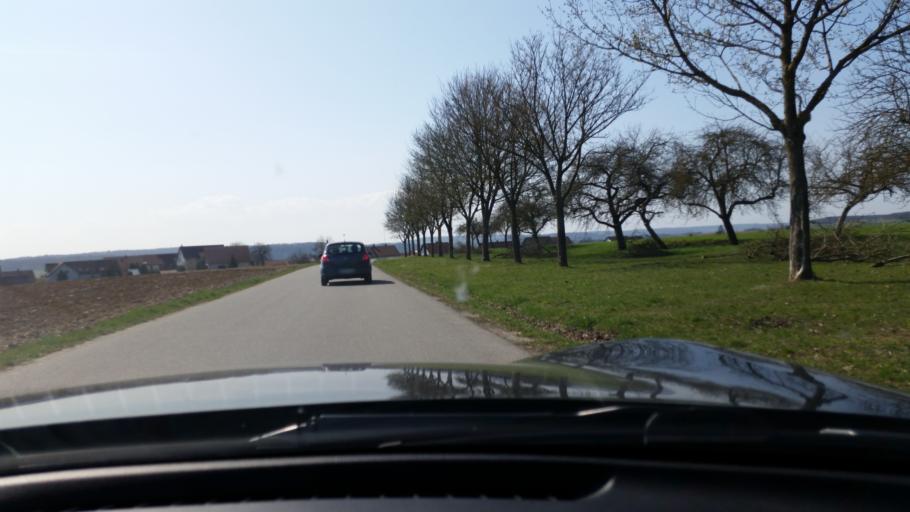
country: DE
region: Baden-Wuerttemberg
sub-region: Regierungsbezirk Stuttgart
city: Krautheim
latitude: 49.3956
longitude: 9.6375
